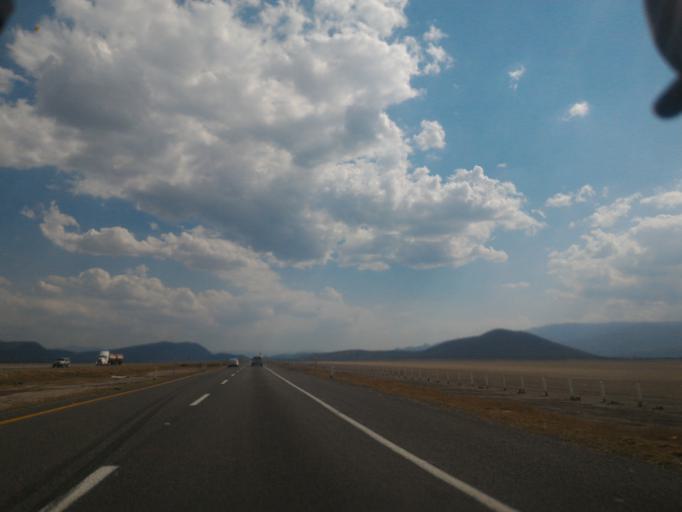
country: MX
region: Jalisco
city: Zacoalco de Torres
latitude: 20.3014
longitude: -103.5590
